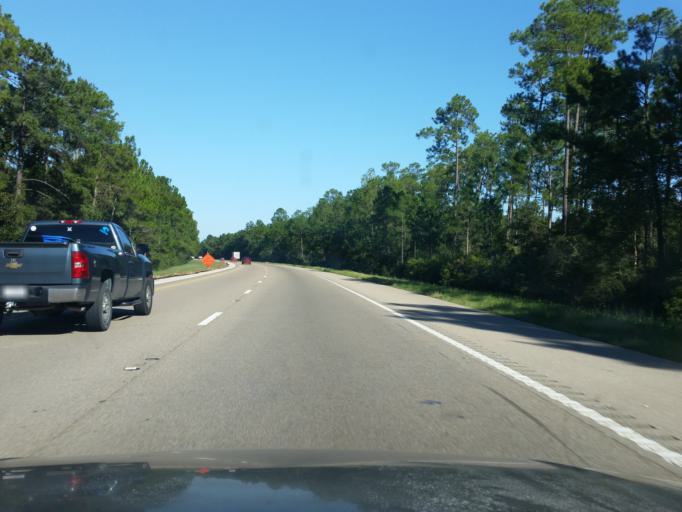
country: US
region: Mississippi
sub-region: Hancock County
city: Pearlington
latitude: 30.3314
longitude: -89.5313
